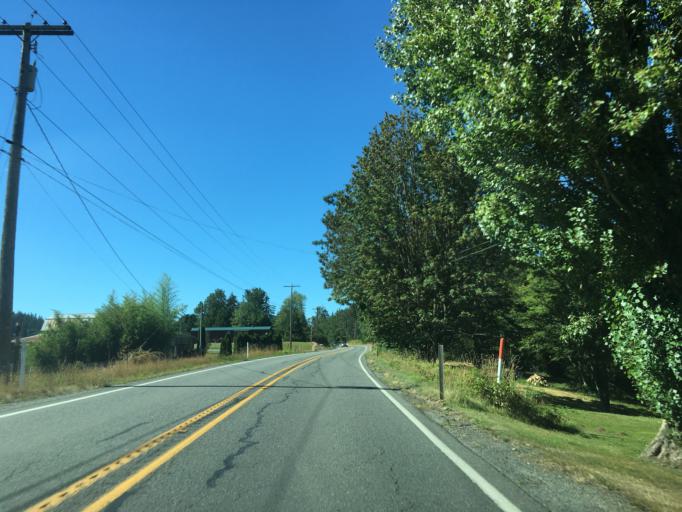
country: US
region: Washington
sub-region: Skagit County
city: Big Lake
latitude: 48.4128
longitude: -122.2487
